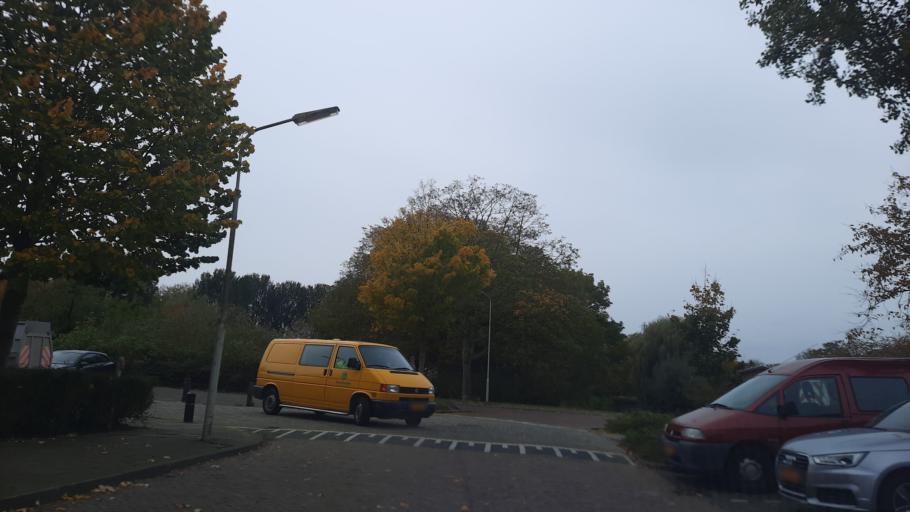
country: NL
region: South Holland
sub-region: Gemeente Gorinchem
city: Gorinchem
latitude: 51.8402
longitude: 4.9608
